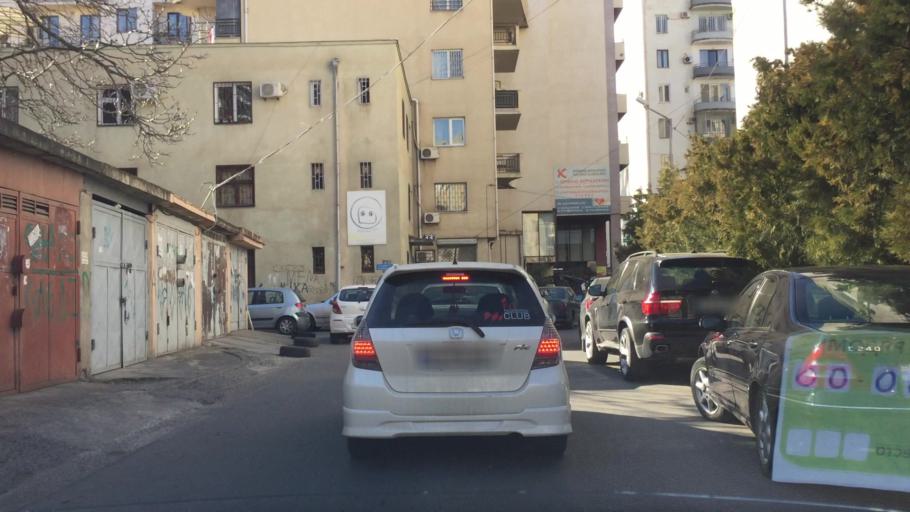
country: GE
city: Tsqnet'i
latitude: 41.7132
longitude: 44.7611
